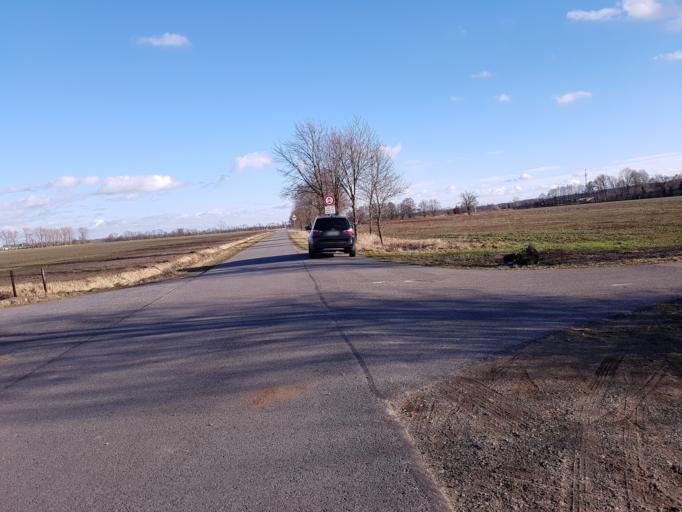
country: DE
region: Brandenburg
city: Groden
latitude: 51.4126
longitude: 13.5759
